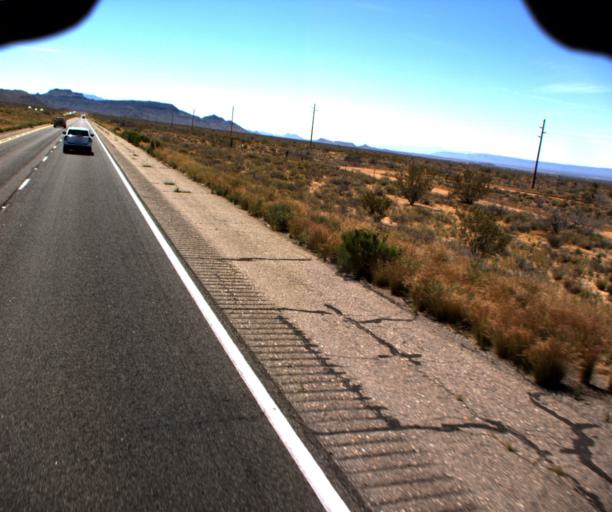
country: US
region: Arizona
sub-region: Mohave County
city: Golden Valley
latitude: 35.2733
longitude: -114.1701
